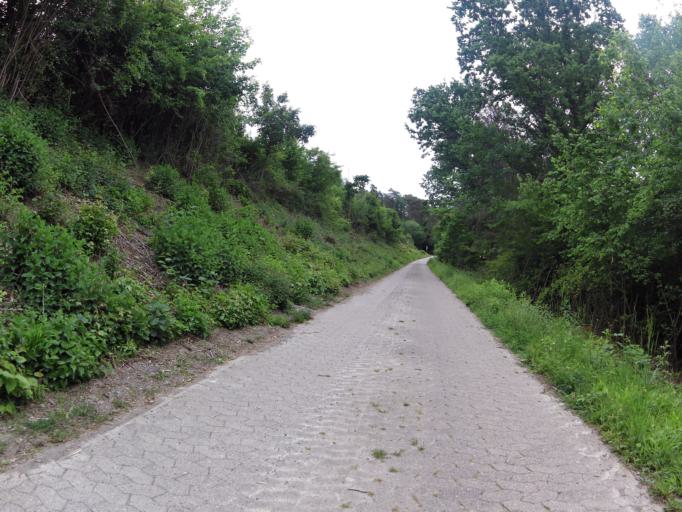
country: DE
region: North Rhine-Westphalia
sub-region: Regierungsbezirk Detmold
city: Hoexter
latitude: 51.7887
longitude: 9.3770
